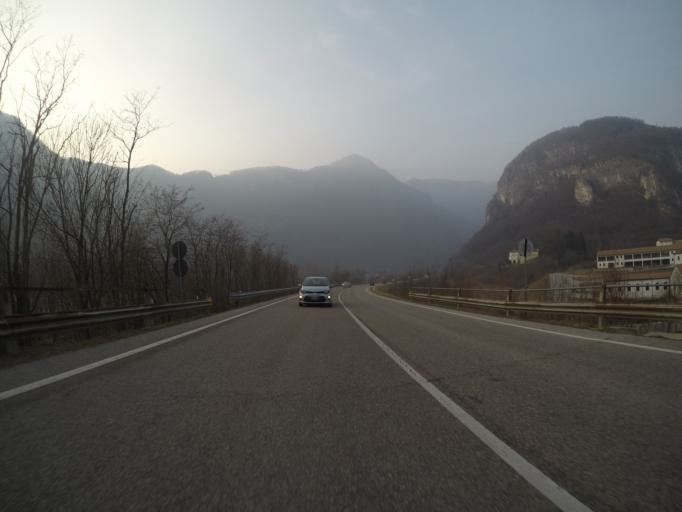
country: IT
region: Veneto
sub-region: Provincia di Belluno
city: Vas
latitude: 45.9370
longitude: 11.9280
